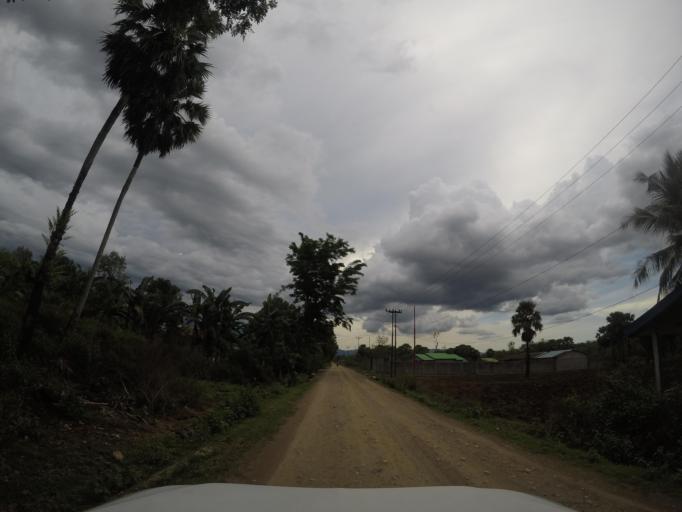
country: TL
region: Bobonaro
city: Maliana
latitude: -8.9937
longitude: 125.2073
